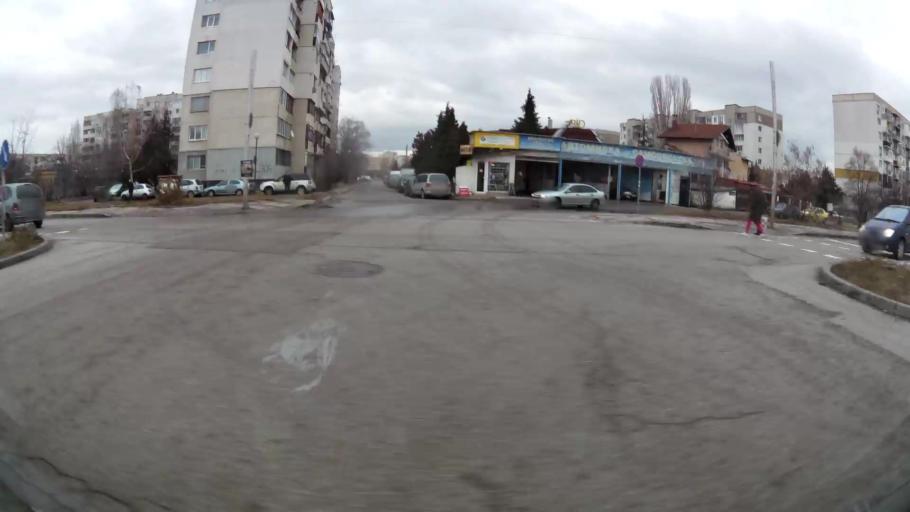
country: BG
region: Sofia-Capital
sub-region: Stolichna Obshtina
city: Sofia
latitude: 42.7296
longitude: 23.2874
